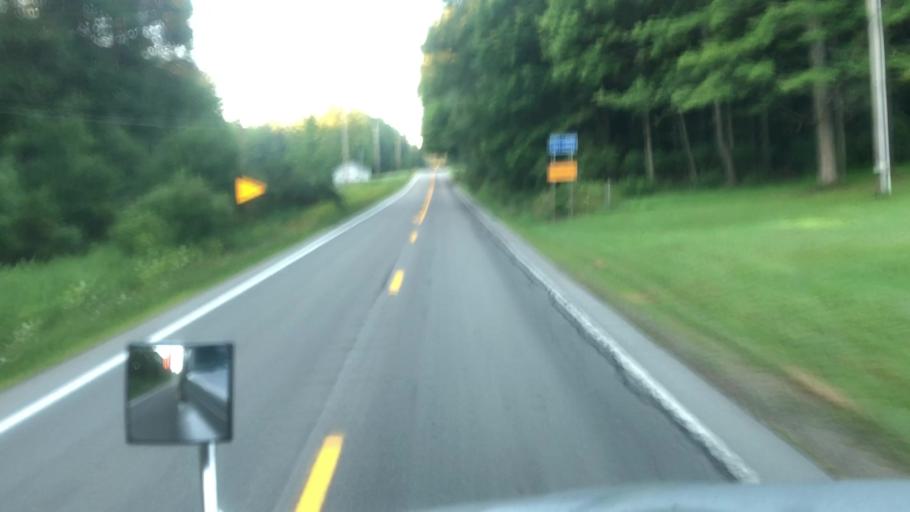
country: US
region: Pennsylvania
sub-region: Crawford County
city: Titusville
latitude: 41.5836
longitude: -79.6098
